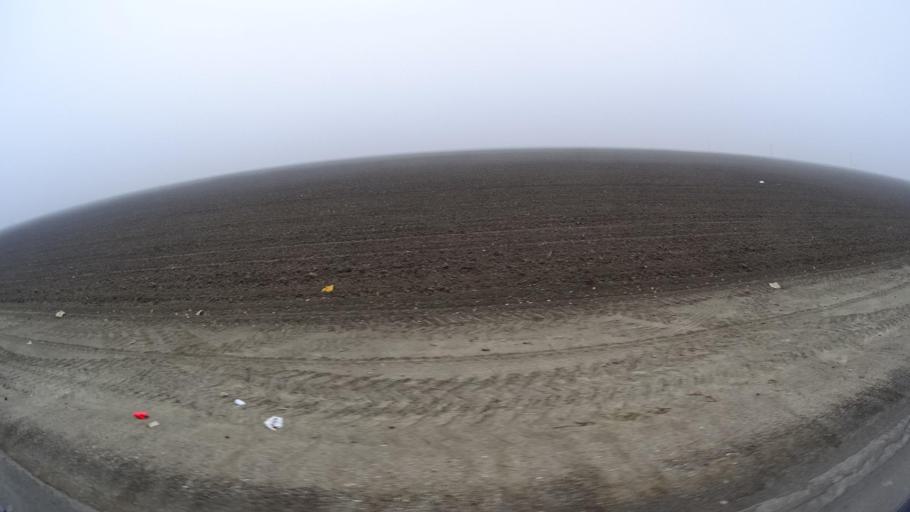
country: US
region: California
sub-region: Kern County
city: Buttonwillow
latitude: 35.4442
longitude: -119.5178
